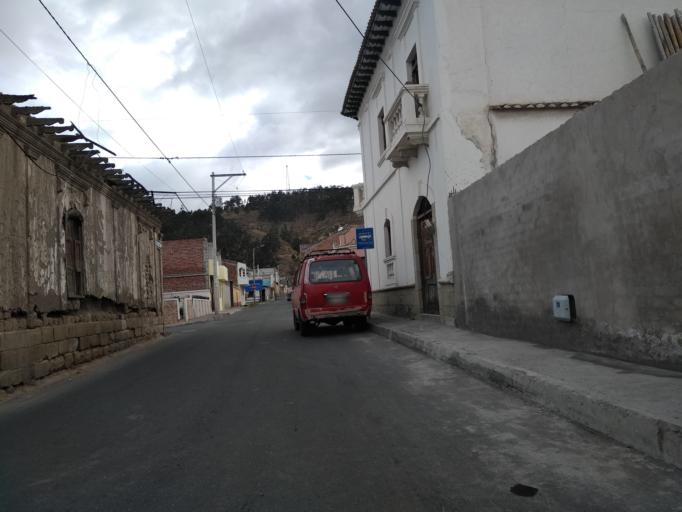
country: EC
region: Chimborazo
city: Riobamba
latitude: -1.6879
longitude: -78.6762
